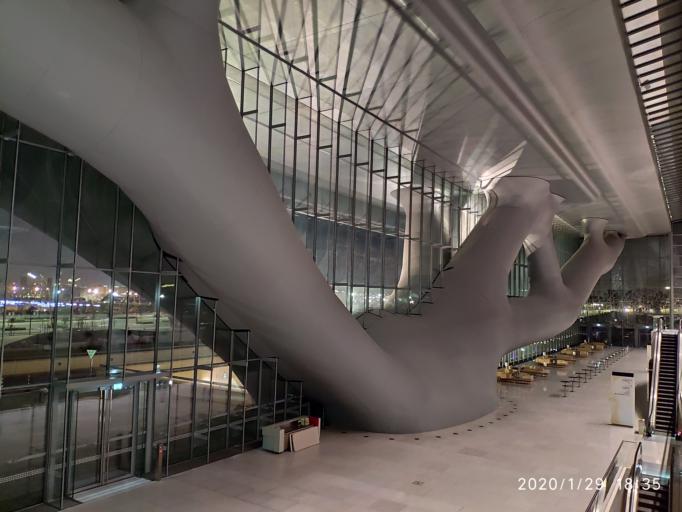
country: QA
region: Baladiyat ar Rayyan
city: Ar Rayyan
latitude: 25.3212
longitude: 51.4372
